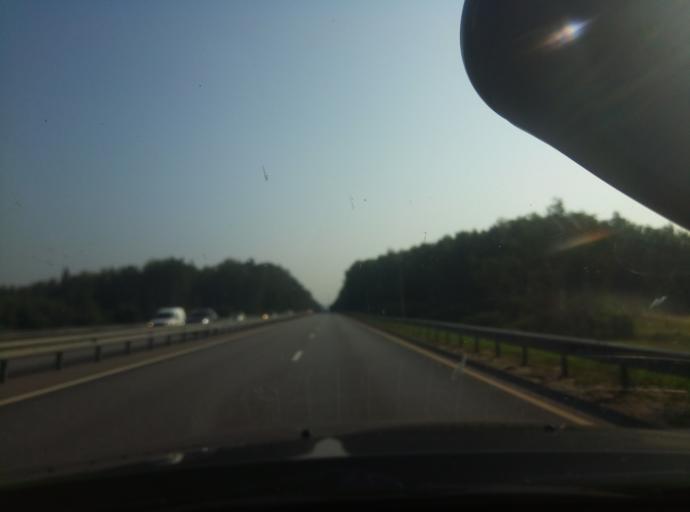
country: RU
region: Kaluga
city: Maloyaroslavets
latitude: 55.0114
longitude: 36.5462
